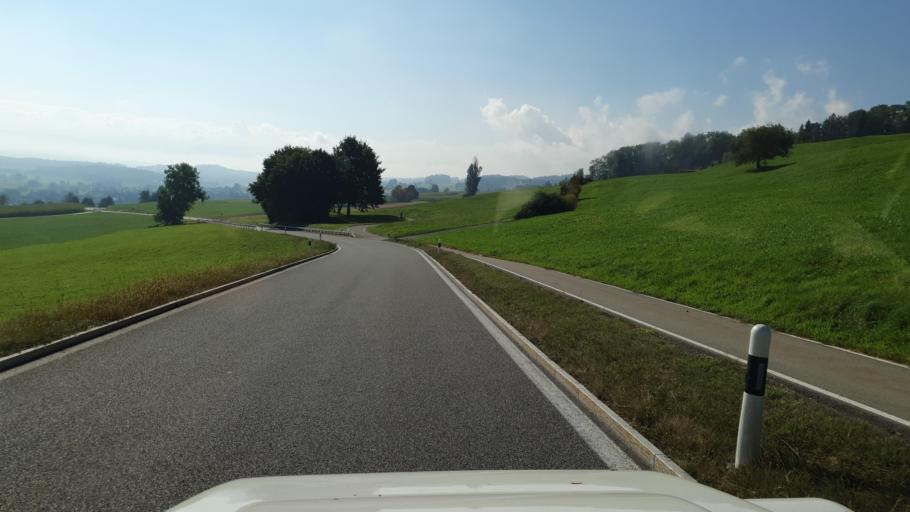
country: CH
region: Aargau
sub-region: Bezirk Muri
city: Waltenschwil
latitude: 47.3088
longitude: 8.2967
